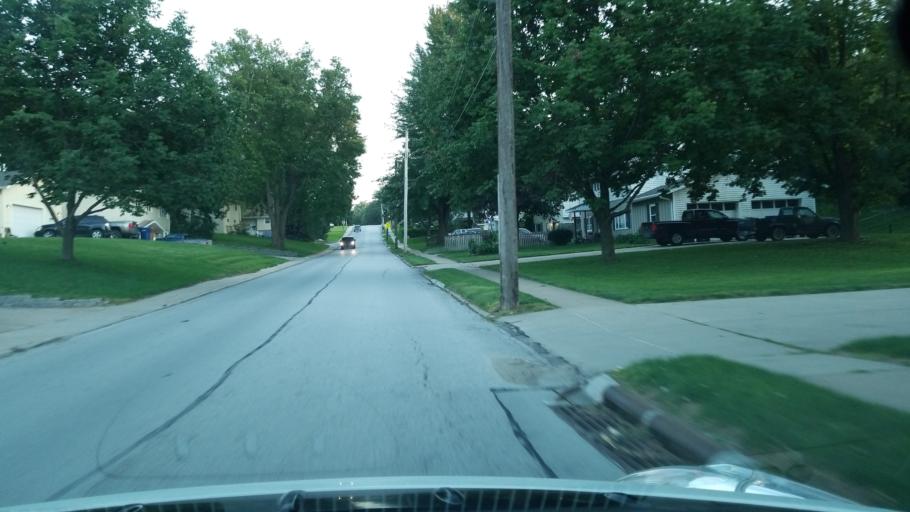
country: US
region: Nebraska
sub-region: Sarpy County
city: Bellevue
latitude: 41.1473
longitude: -95.9016
